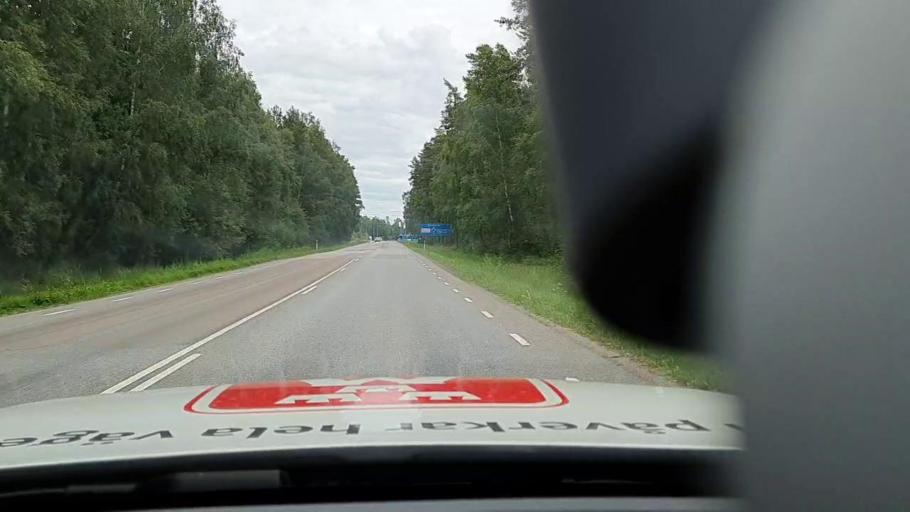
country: SE
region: Vaestra Goetaland
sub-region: Lidkopings Kommun
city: Lidkoping
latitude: 58.4950
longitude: 13.1359
